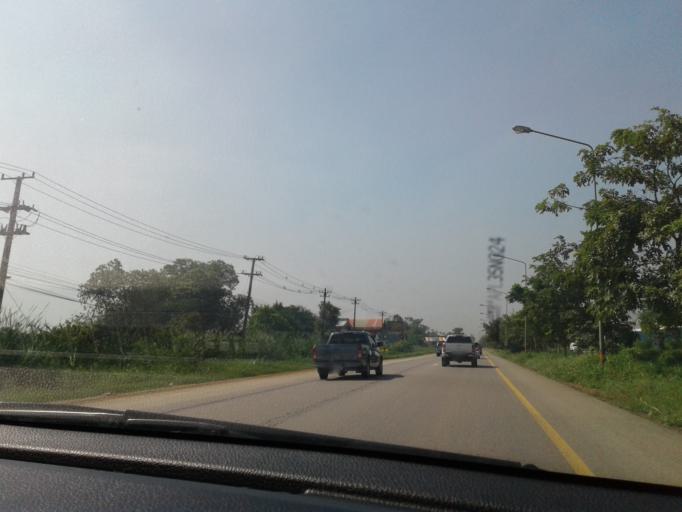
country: TH
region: Ratchaburi
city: Ban Pong
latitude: 13.7674
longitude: 99.9308
